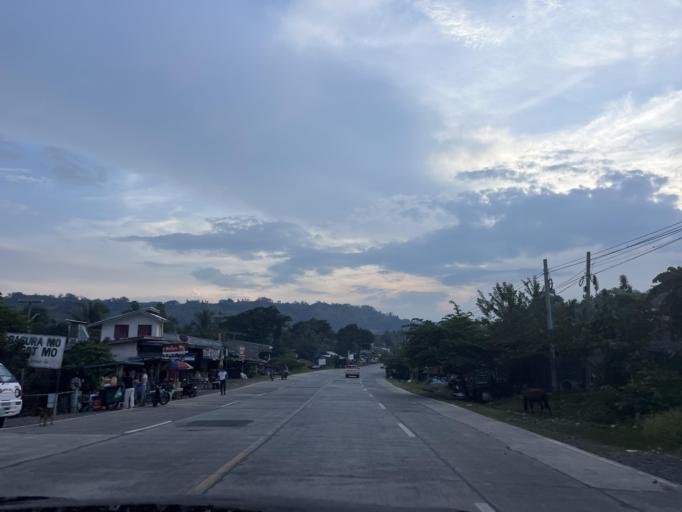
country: PH
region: Northern Mindanao
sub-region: Province of Bukidnon
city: Dalorong
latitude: 7.6090
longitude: 125.1160
